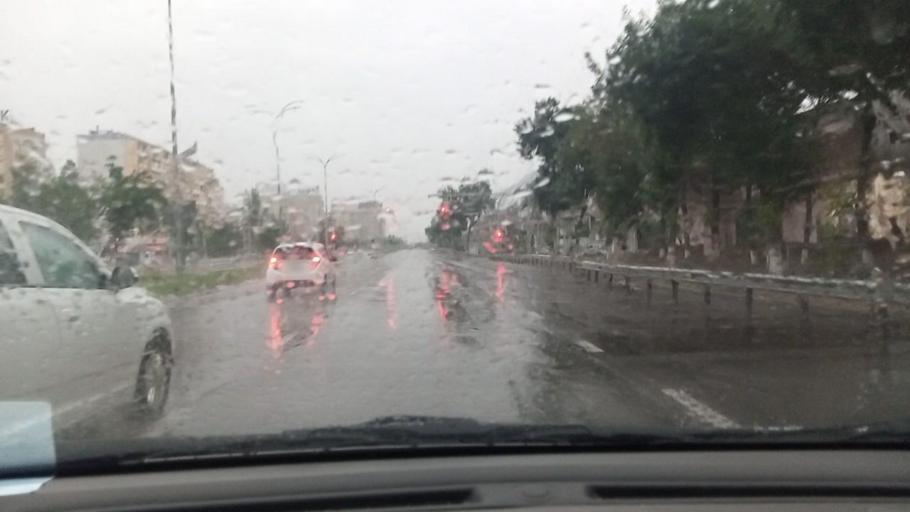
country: UZ
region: Toshkent
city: Salor
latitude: 41.2936
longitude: 69.3551
